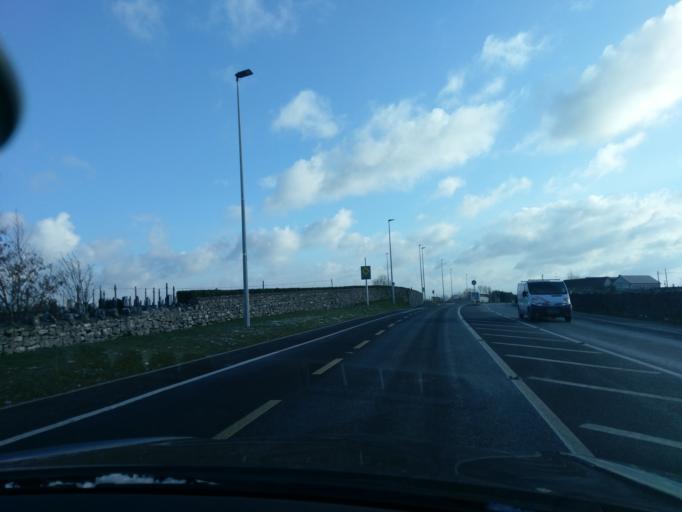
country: IE
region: Connaught
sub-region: County Galway
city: Gort
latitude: 53.1436
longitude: -8.8041
